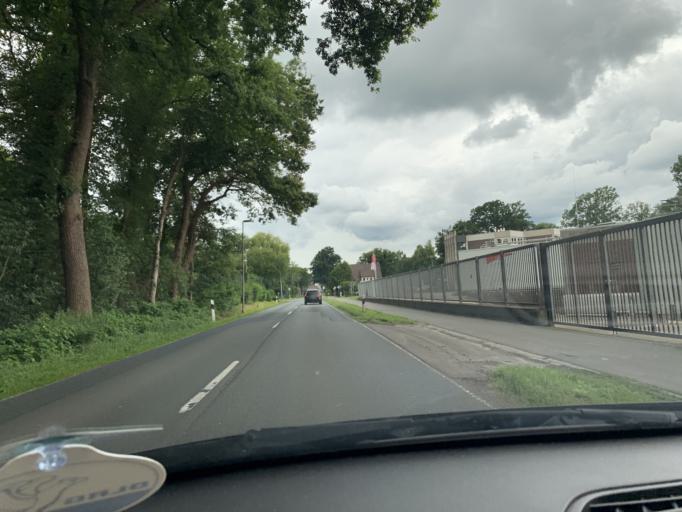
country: DE
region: Lower Saxony
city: Edewecht
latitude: 53.1177
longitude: 7.9476
